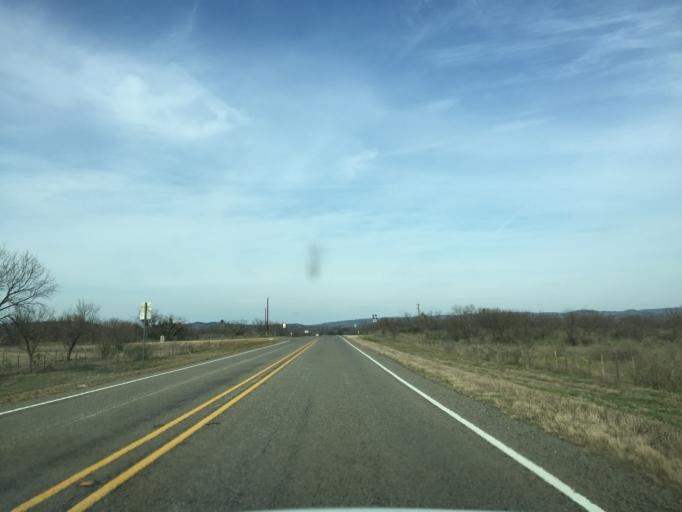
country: US
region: Texas
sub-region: Llano County
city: Llano
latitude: 30.5420
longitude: -98.7048
